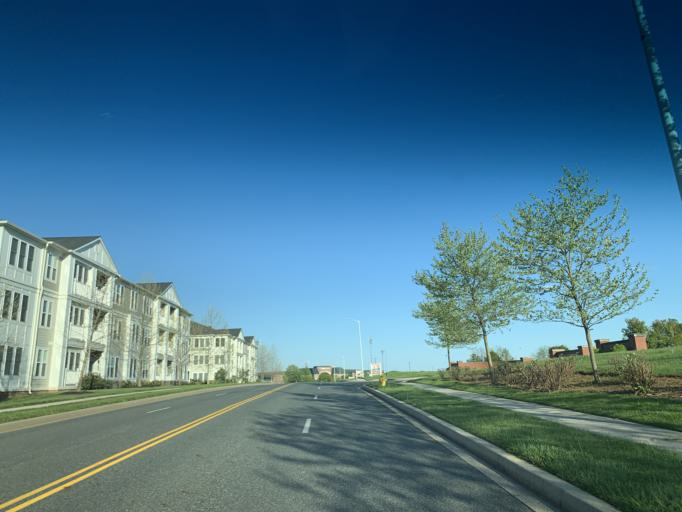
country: US
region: Maryland
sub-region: Harford County
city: Aberdeen
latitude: 39.5328
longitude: -76.1909
